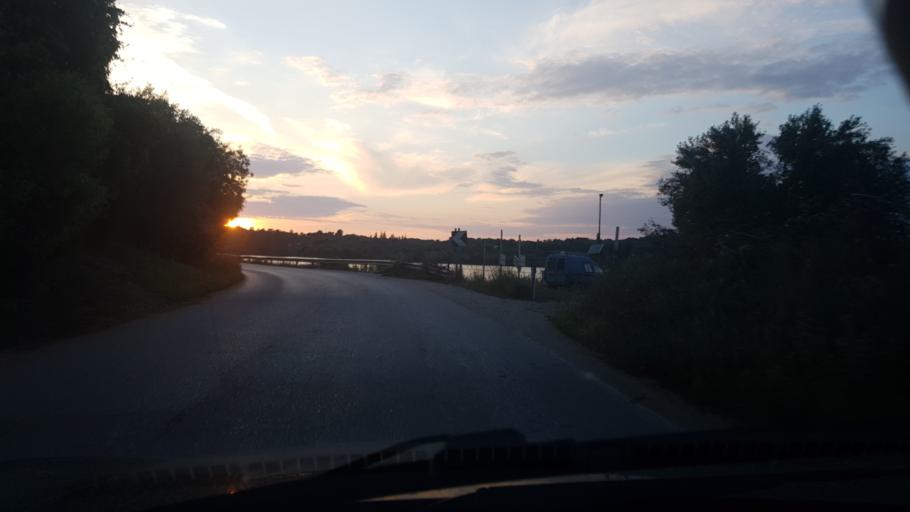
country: GR
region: West Greece
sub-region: Nomos Aitolias kai Akarnanias
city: Vonitsa
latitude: 38.9175
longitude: 20.8672
